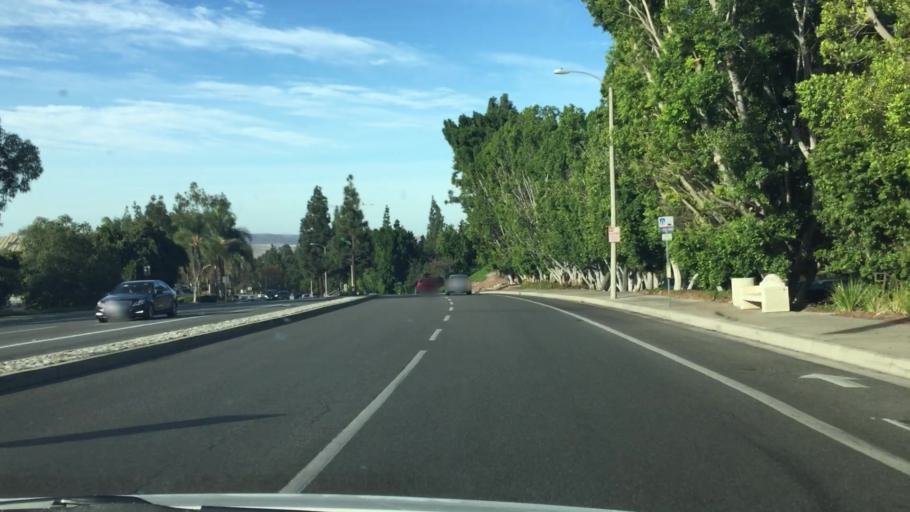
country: US
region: California
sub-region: Orange County
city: Lake Forest
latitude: 33.6482
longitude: -117.6822
